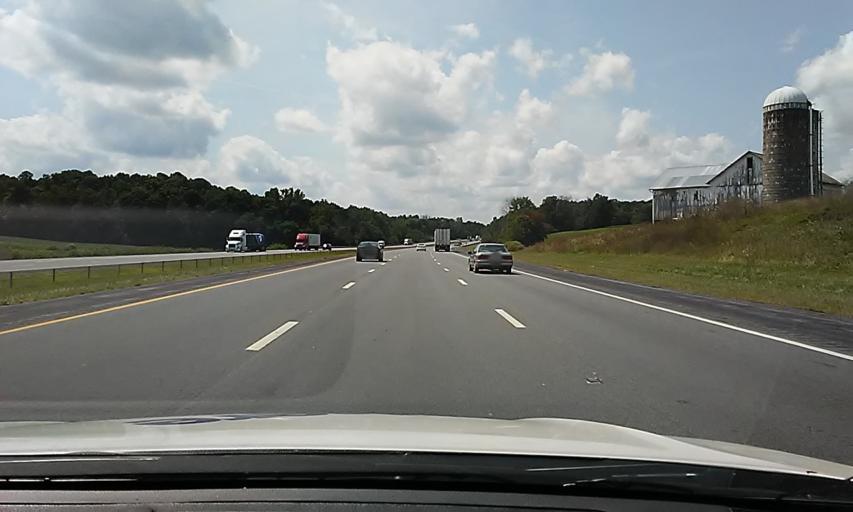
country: US
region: Ohio
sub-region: Richland County
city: Lexington
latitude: 40.5773
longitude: -82.6059
